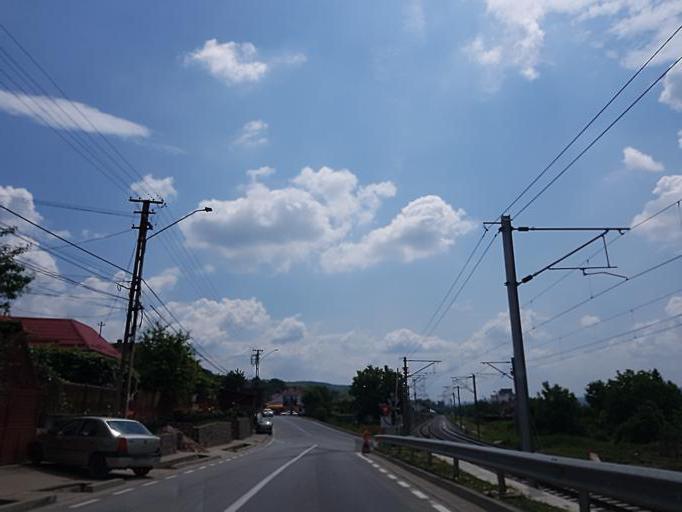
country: RO
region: Alba
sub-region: Municipiul Blaj
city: Veza
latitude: 46.1752
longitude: 23.9362
